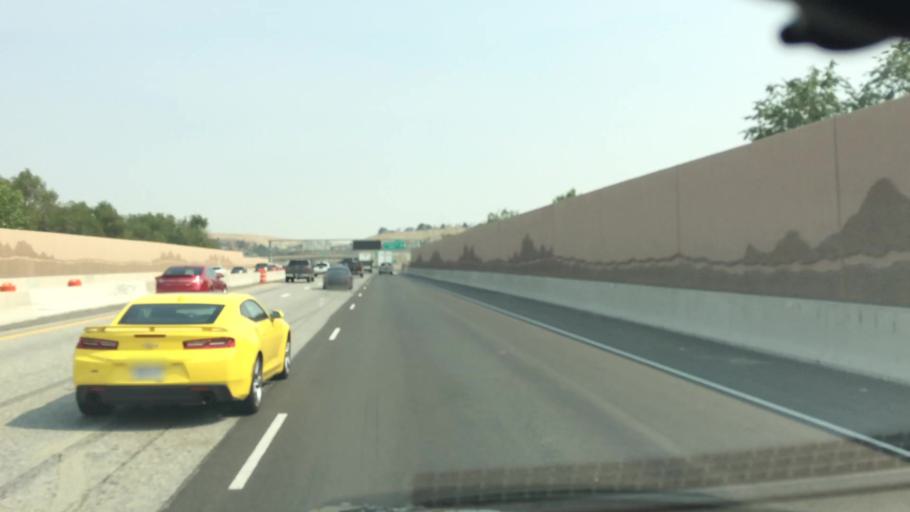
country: US
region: Nevada
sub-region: Washoe County
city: Reno
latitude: 39.5499
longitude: -119.7878
